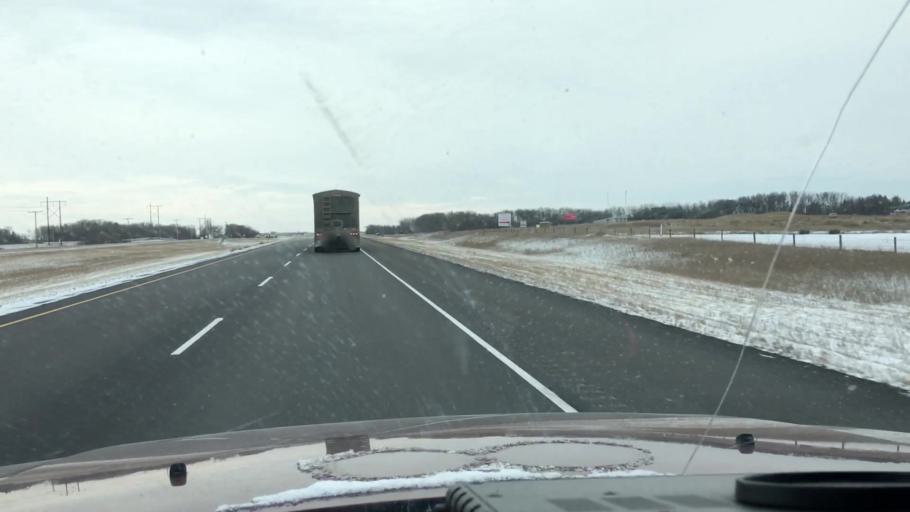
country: CA
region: Saskatchewan
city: Saskatoon
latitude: 51.9442
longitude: -106.5420
